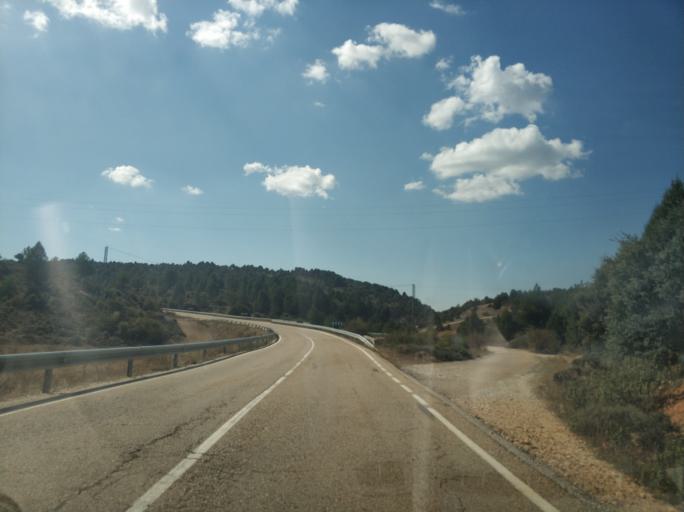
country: ES
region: Castille and Leon
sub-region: Provincia de Soria
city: Casarejos
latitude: 41.7888
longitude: -3.0326
